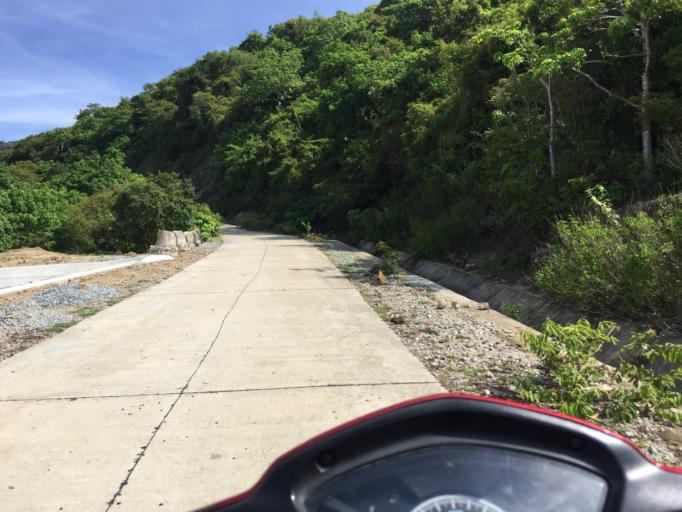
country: VN
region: Quang Nam
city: Hoi An
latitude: 15.9337
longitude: 108.5313
